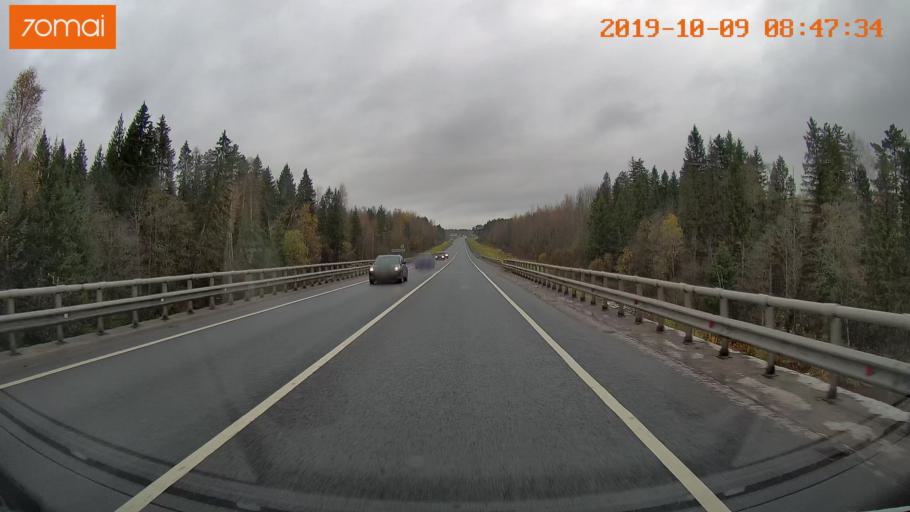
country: RU
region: Vologda
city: Vologda
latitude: 59.0660
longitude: 40.0437
